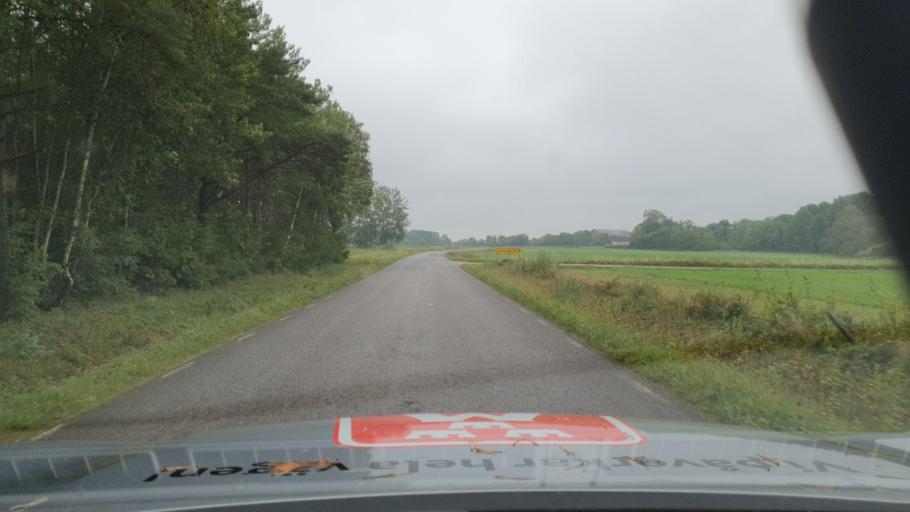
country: SE
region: Gotland
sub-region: Gotland
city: Visby
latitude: 57.7834
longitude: 18.5160
